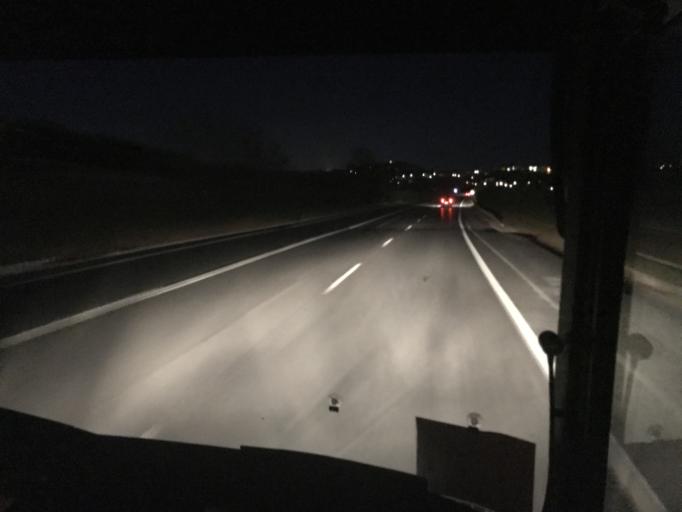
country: GR
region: Crete
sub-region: Nomos Irakleiou
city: Skalanion
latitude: 35.2682
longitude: 25.1849
